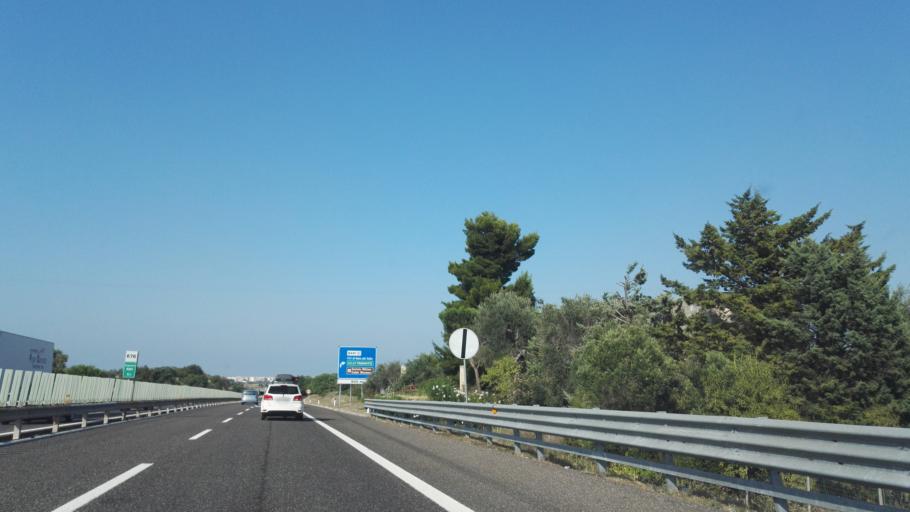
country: IT
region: Apulia
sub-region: Provincia di Bari
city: Modugno
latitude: 41.0930
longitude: 16.8172
